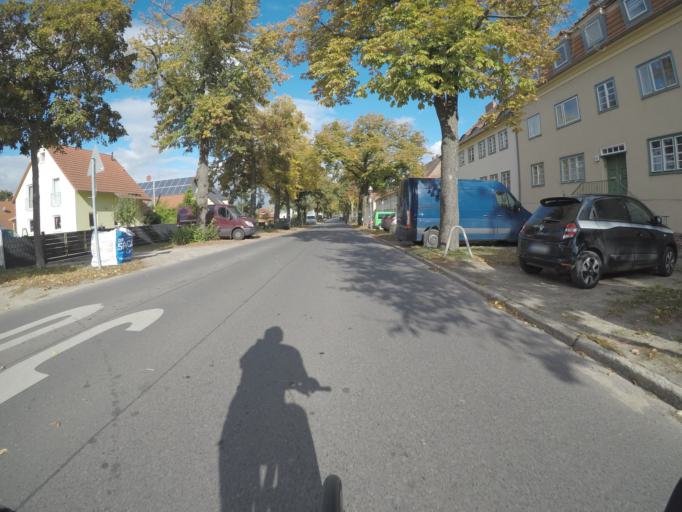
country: DE
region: Berlin
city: Staaken
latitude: 52.5399
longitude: 13.1429
